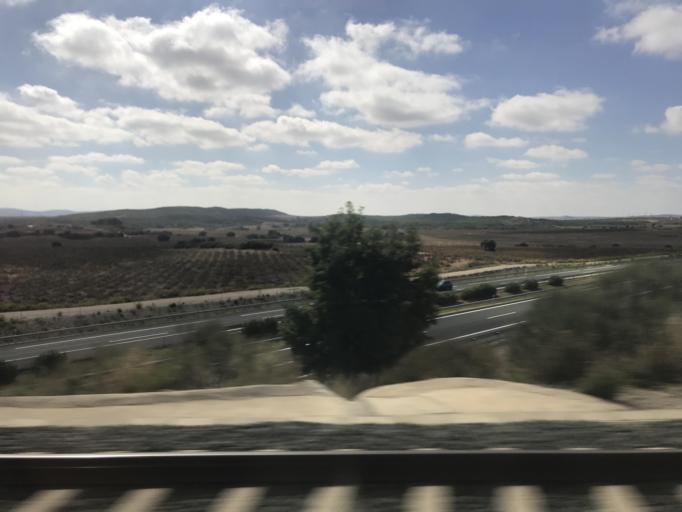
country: ES
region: Castille-La Mancha
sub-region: Provincia de Albacete
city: Bonete
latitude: 38.8794
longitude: -1.2562
